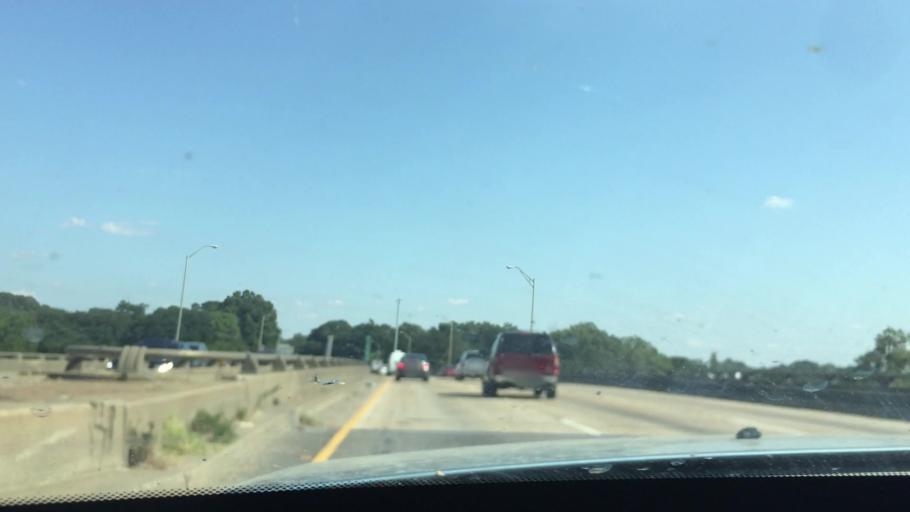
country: US
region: Louisiana
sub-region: East Baton Rouge Parish
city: Baton Rouge
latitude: 30.4271
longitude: -91.1688
